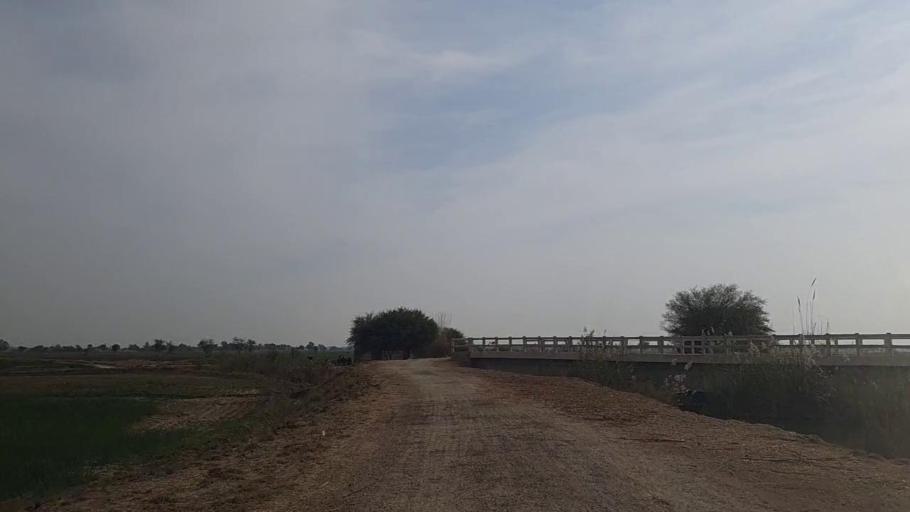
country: PK
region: Sindh
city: Daur
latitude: 26.4439
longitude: 68.4213
